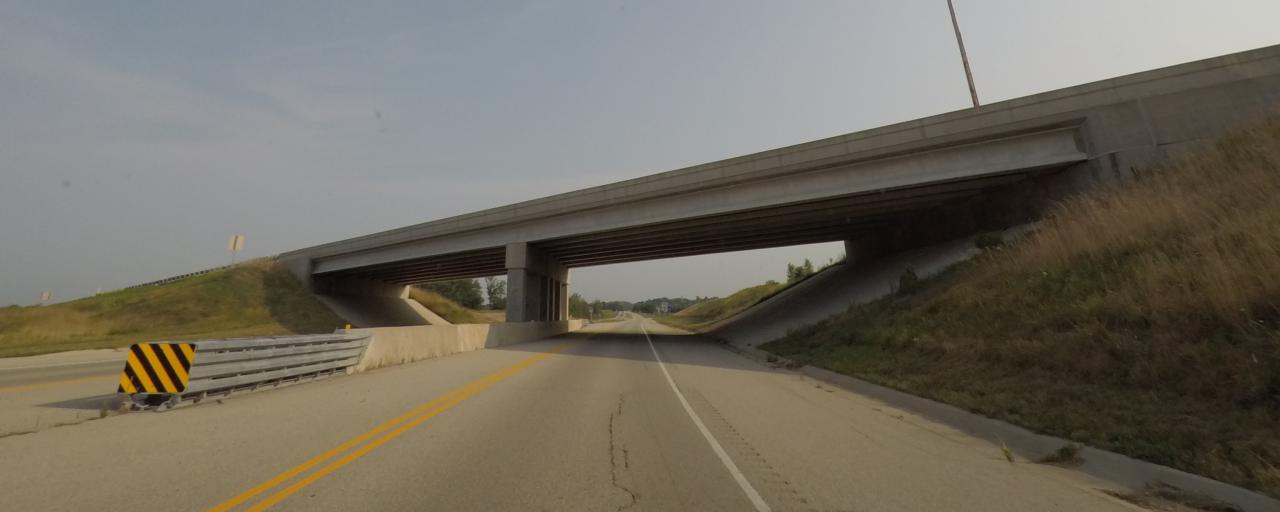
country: US
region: Wisconsin
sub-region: Dane County
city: Deerfield
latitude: 43.0262
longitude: -89.0772
